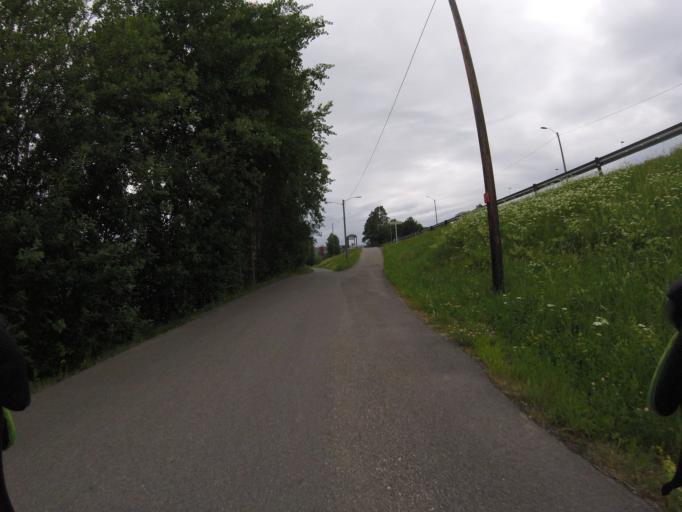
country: NO
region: Akershus
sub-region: Skedsmo
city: Lillestrom
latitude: 59.9791
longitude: 11.0150
